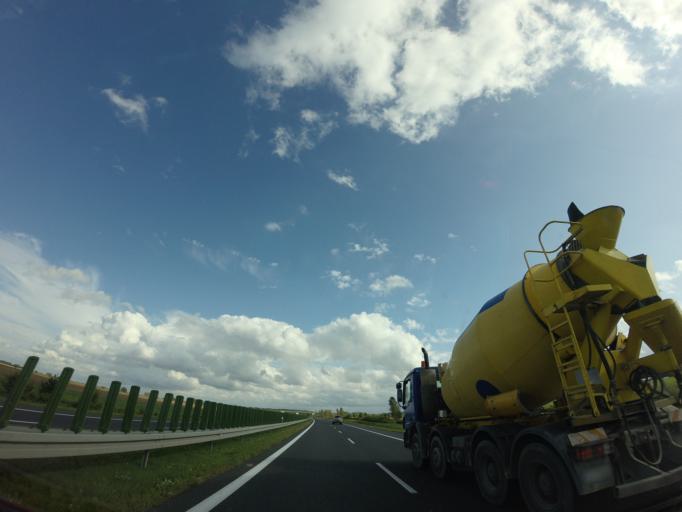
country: PL
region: West Pomeranian Voivodeship
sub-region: Powiat pyrzycki
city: Warnice
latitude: 53.3168
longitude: 14.9763
